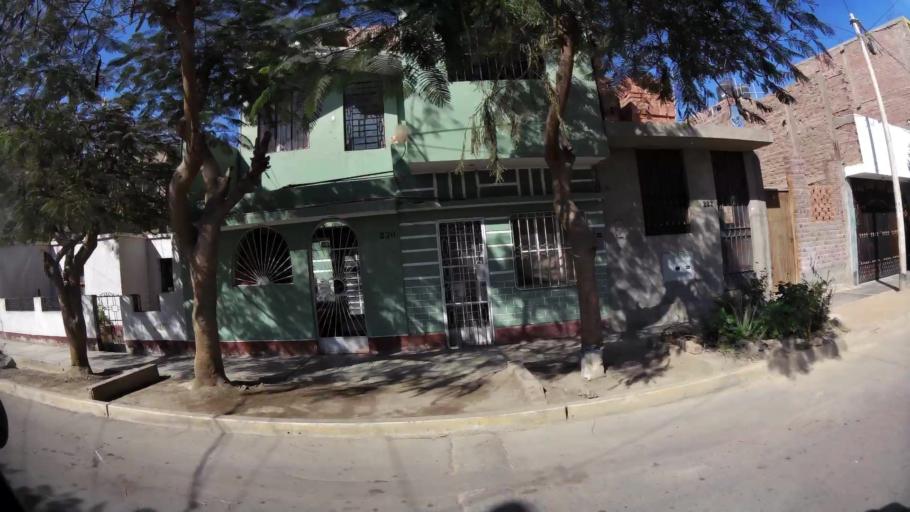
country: PE
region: Ica
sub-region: Provincia de Ica
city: La Tinguina
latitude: -14.0364
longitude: -75.7110
